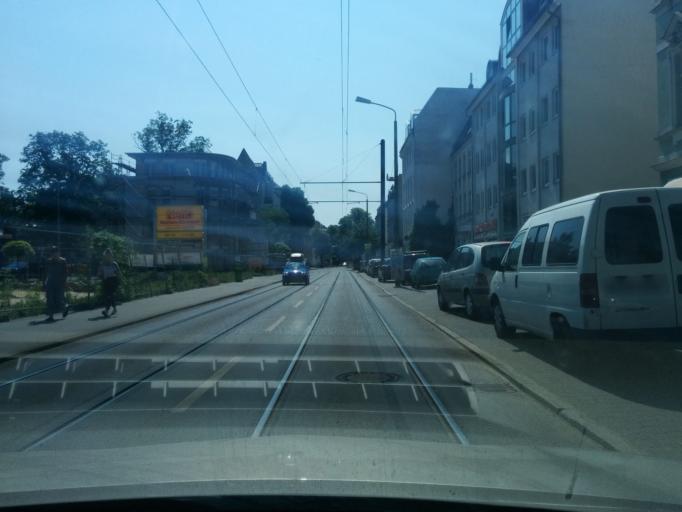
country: DE
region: Berlin
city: Grunau
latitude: 52.4180
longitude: 13.5800
